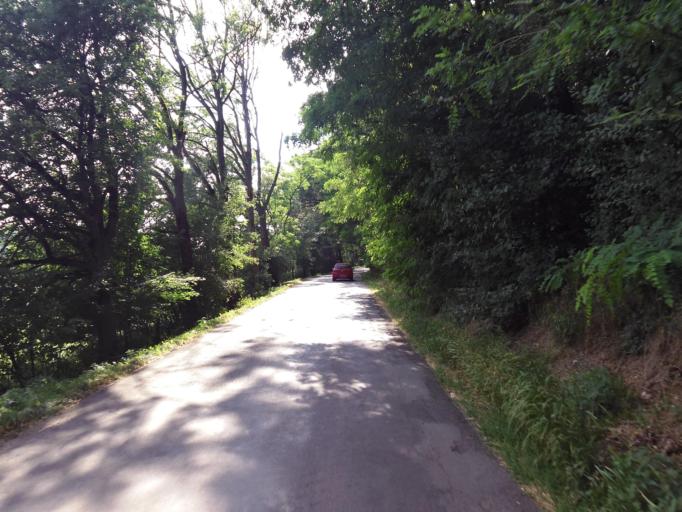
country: CZ
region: Central Bohemia
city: Mnichovo Hradiste
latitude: 50.5613
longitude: 14.9848
